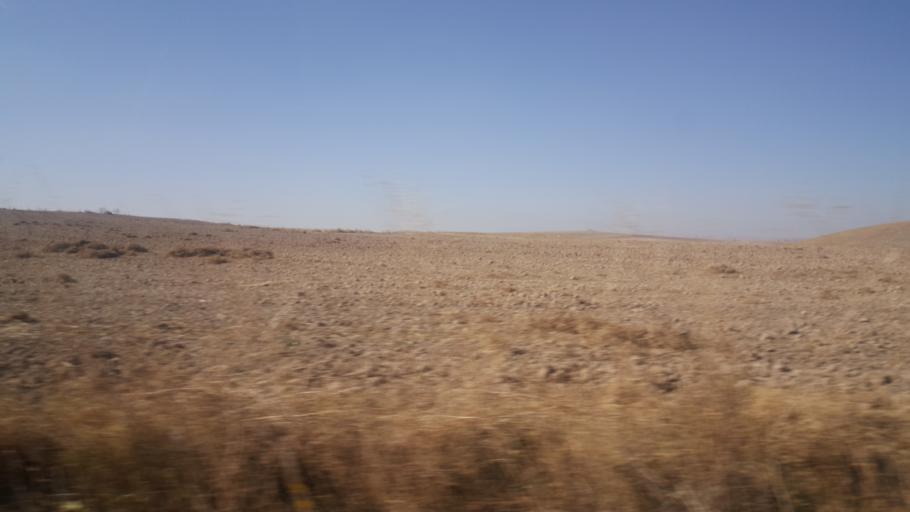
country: TR
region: Konya
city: Celtik
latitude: 39.0886
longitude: 32.0553
